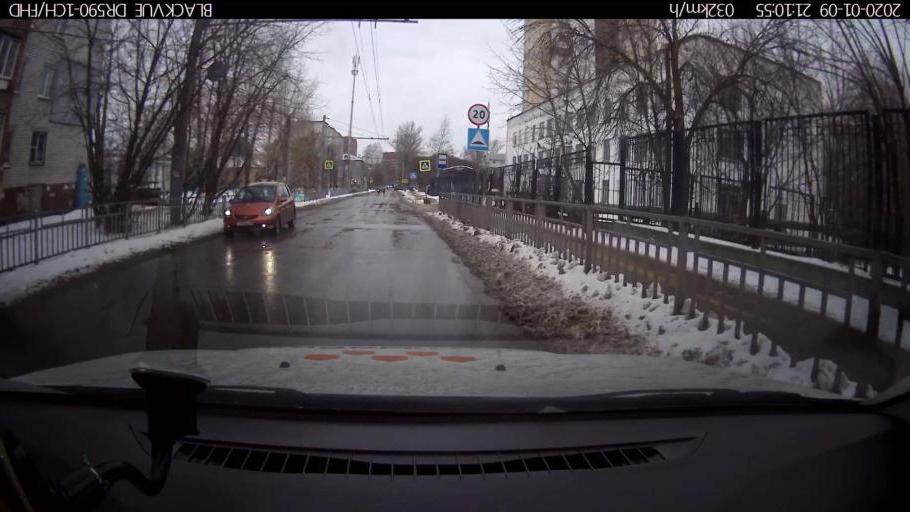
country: RU
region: Nizjnij Novgorod
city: Gorbatovka
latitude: 56.2890
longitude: 43.8528
